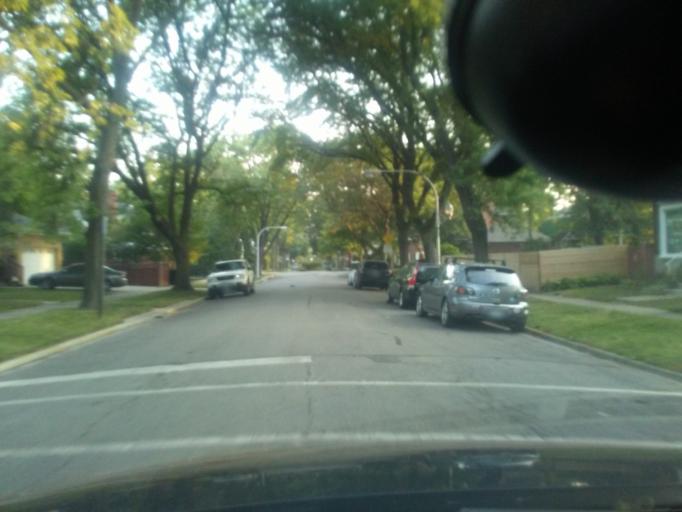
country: US
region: Illinois
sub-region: Cook County
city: Lincolnwood
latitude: 41.9795
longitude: -87.7015
